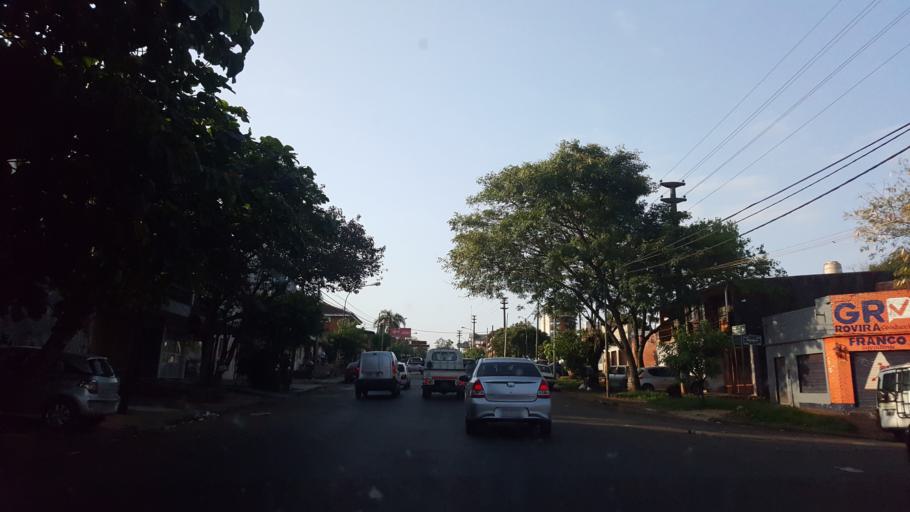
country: AR
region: Misiones
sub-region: Departamento de Capital
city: Posadas
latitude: -27.3906
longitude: -55.8970
